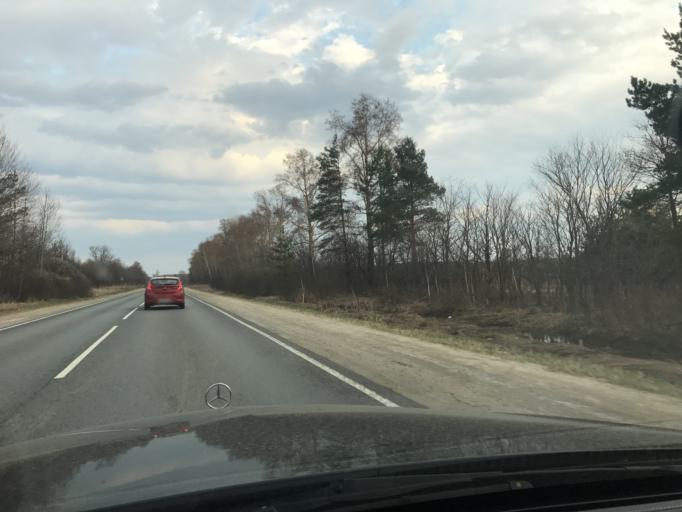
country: RU
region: Vladimir
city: Murom
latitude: 55.6429
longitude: 41.8438
